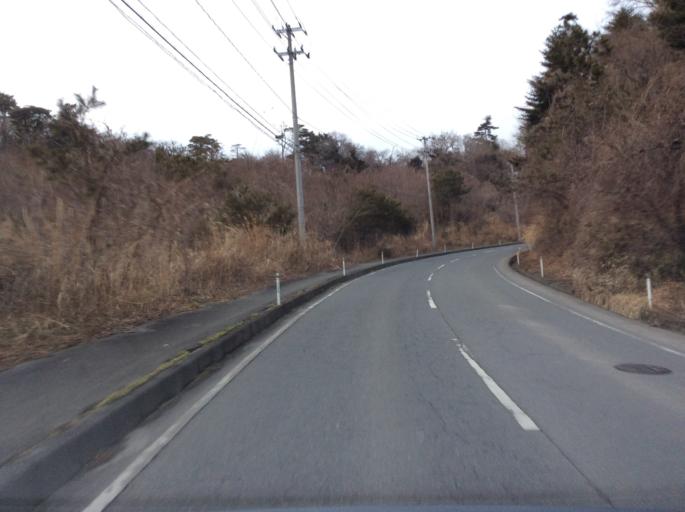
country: JP
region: Fukushima
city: Iwaki
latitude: 37.1168
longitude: 140.9767
